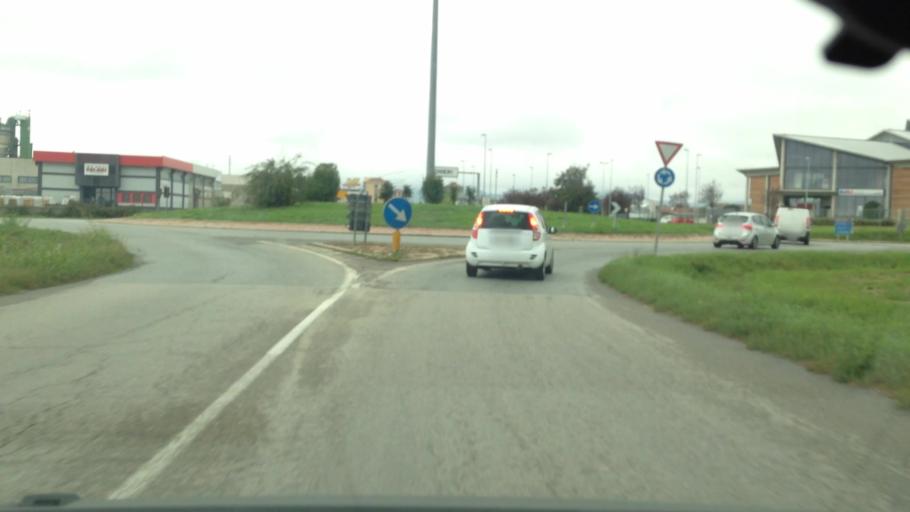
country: IT
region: Piedmont
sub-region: Provincia di Torino
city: Chieri
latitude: 44.9998
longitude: 7.8481
